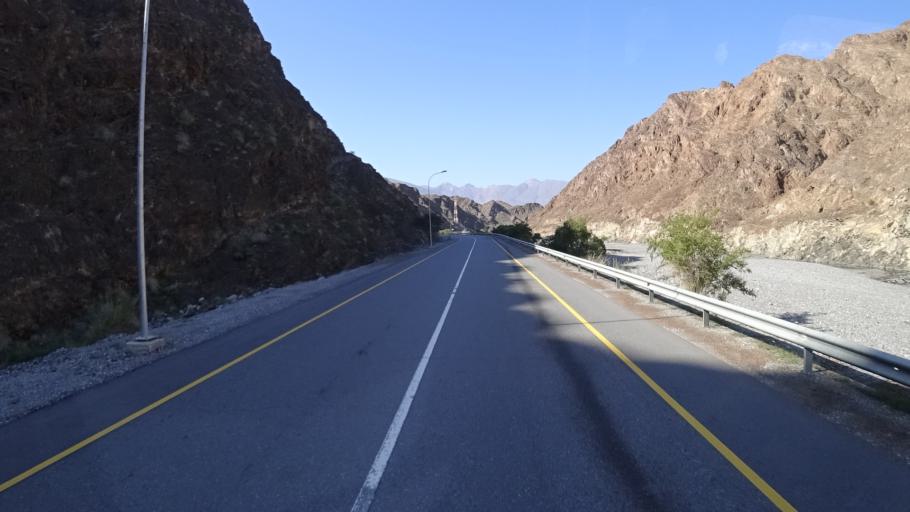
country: OM
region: Al Batinah
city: Bayt al `Awabi
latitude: 23.3234
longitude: 57.6142
